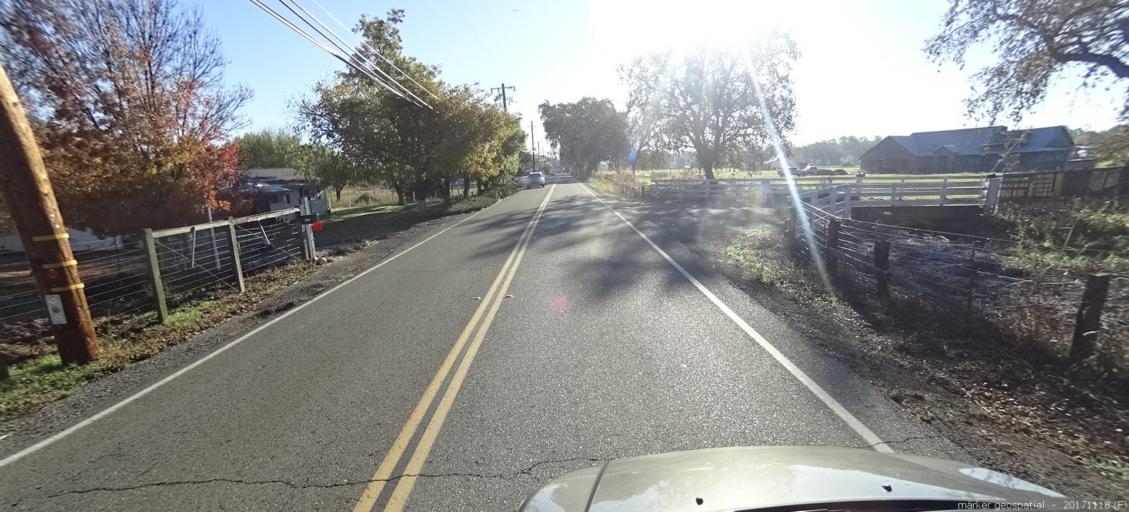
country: US
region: California
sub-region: Shasta County
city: Anderson
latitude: 40.4497
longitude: -122.2647
